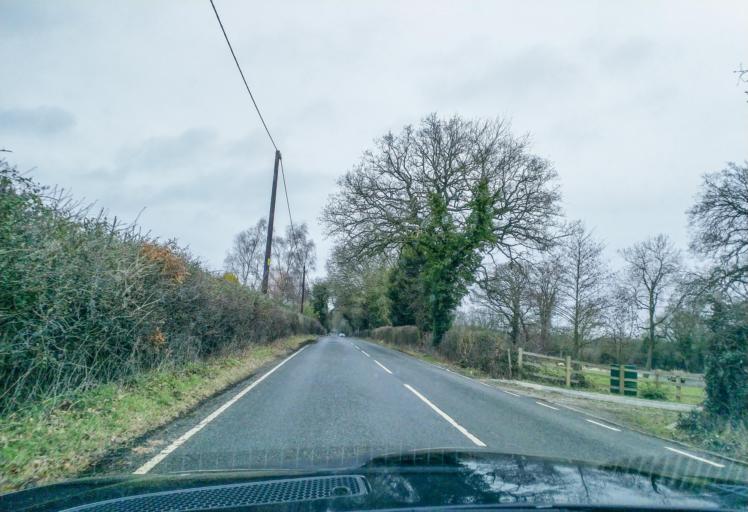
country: GB
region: England
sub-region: Warwickshire
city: Wroxall
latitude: 52.3148
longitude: -1.6747
